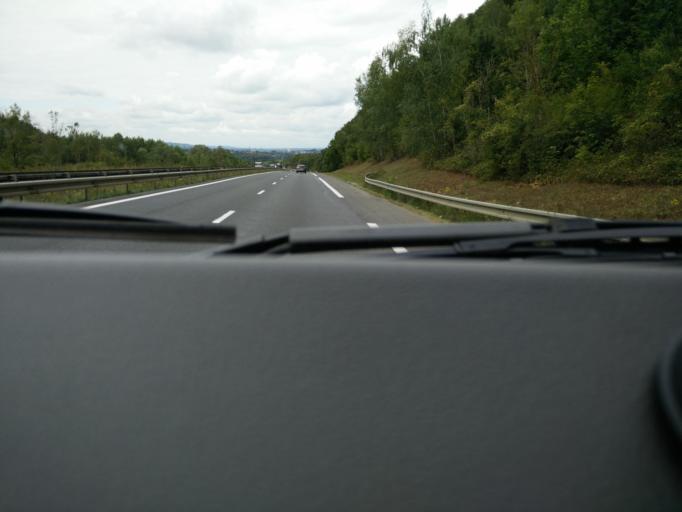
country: FR
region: Champagne-Ardenne
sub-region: Departement des Ardennes
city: Lumes
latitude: 49.7346
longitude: 4.7978
